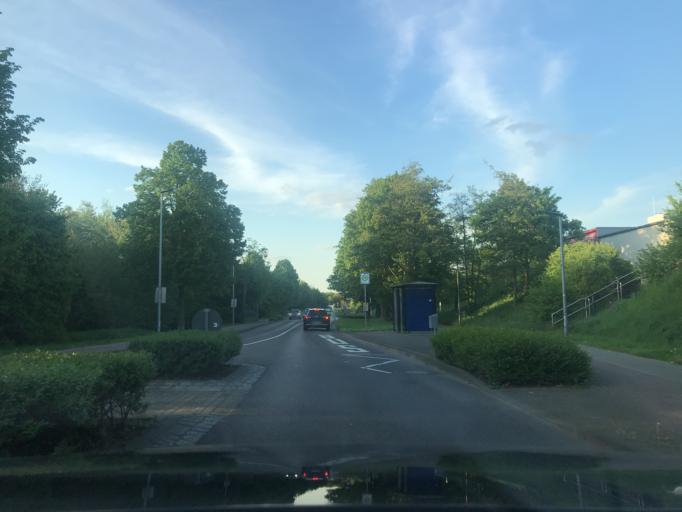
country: DE
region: North Rhine-Westphalia
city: Erkelenz
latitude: 51.0902
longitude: 6.3191
